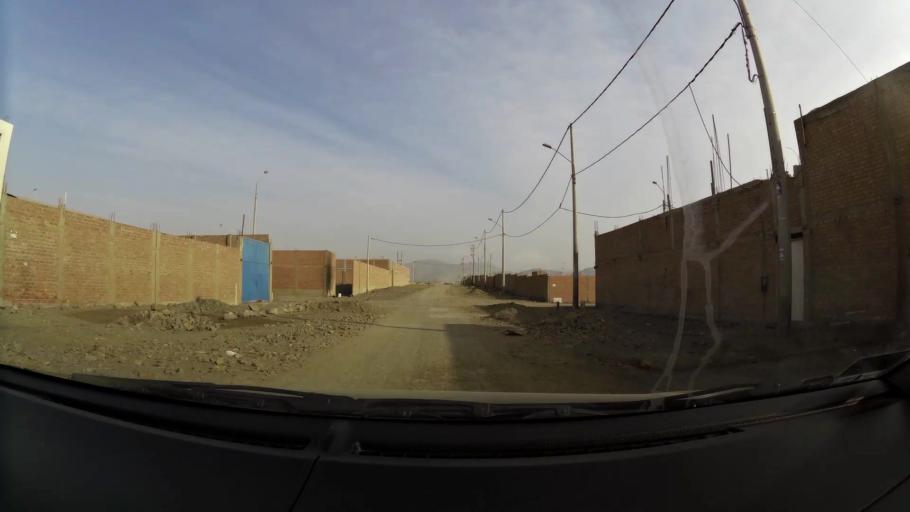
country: PE
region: Lima
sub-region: Lima
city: Santa Rosa
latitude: -11.7532
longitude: -77.1599
